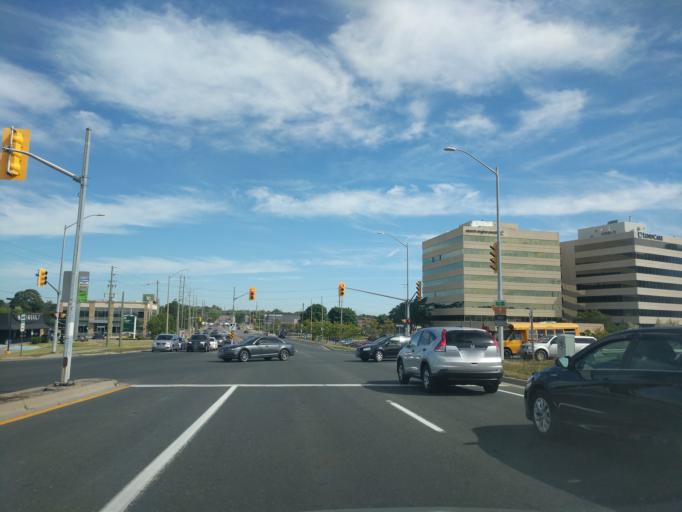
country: CA
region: Ontario
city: Ajax
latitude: 43.8318
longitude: -79.0889
